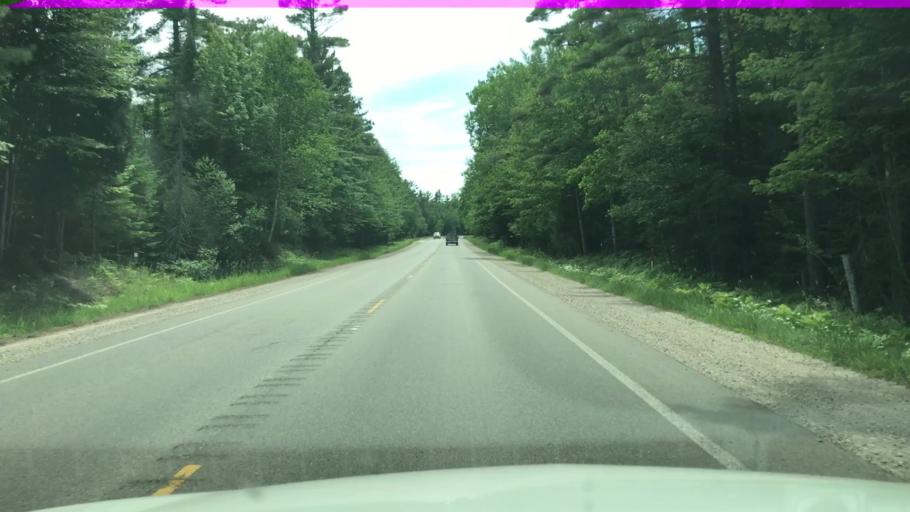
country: US
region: Michigan
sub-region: Schoolcraft County
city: Manistique
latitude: 45.9427
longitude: -86.3297
